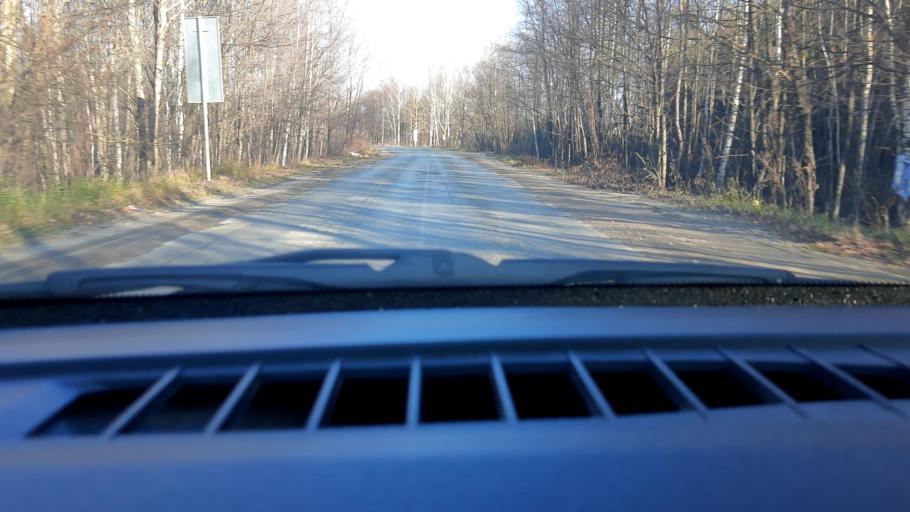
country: RU
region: Nizjnij Novgorod
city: Neklyudovo
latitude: 56.4246
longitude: 43.9253
